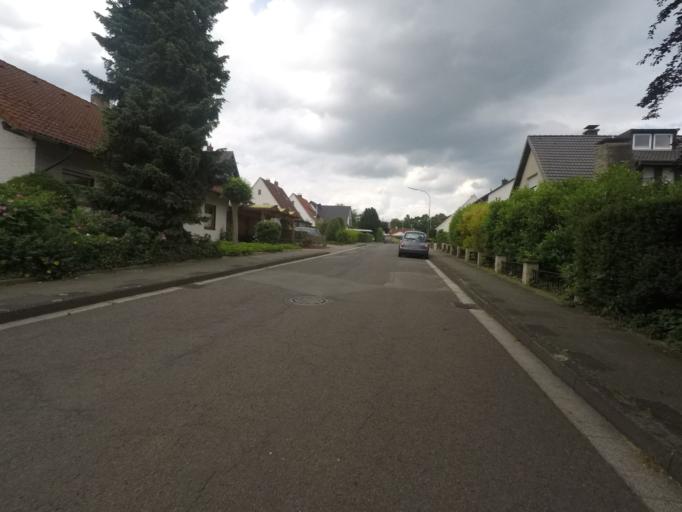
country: DE
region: North Rhine-Westphalia
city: Buende
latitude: 52.2039
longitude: 8.5519
